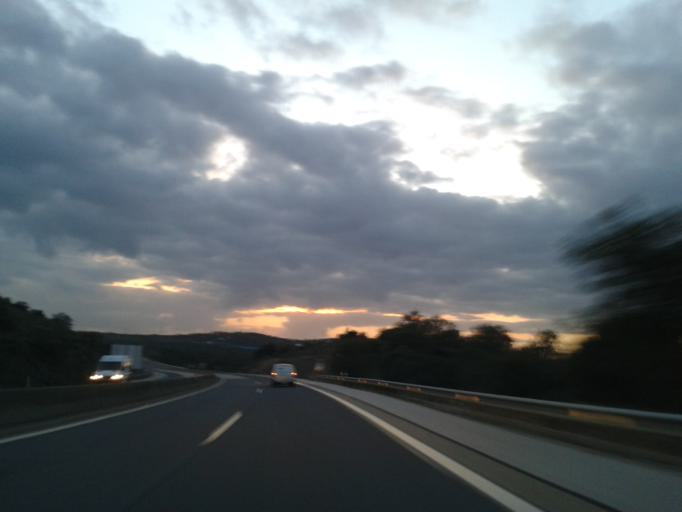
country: PT
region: Faro
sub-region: Loule
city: Boliqueime
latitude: 37.1620
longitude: -8.1971
